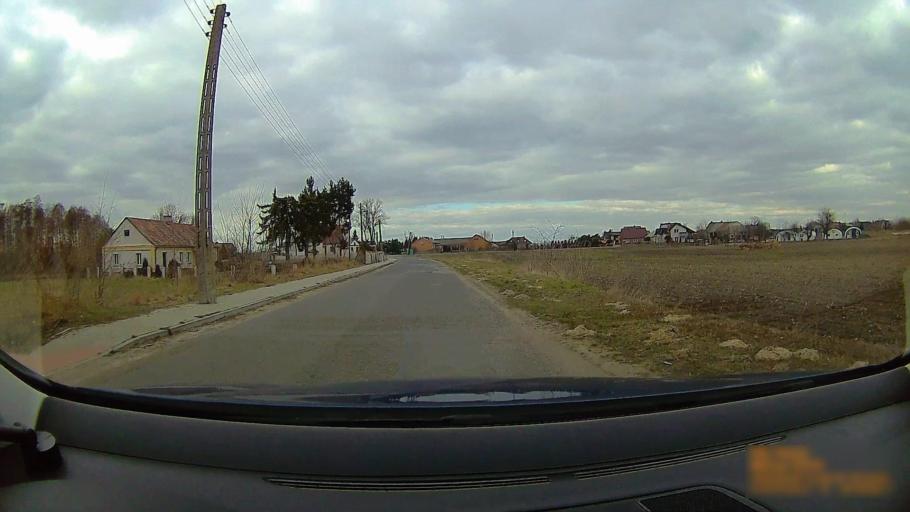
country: PL
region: Greater Poland Voivodeship
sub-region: Powiat koninski
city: Rzgow Pierwszy
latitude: 52.1321
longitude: 18.0585
